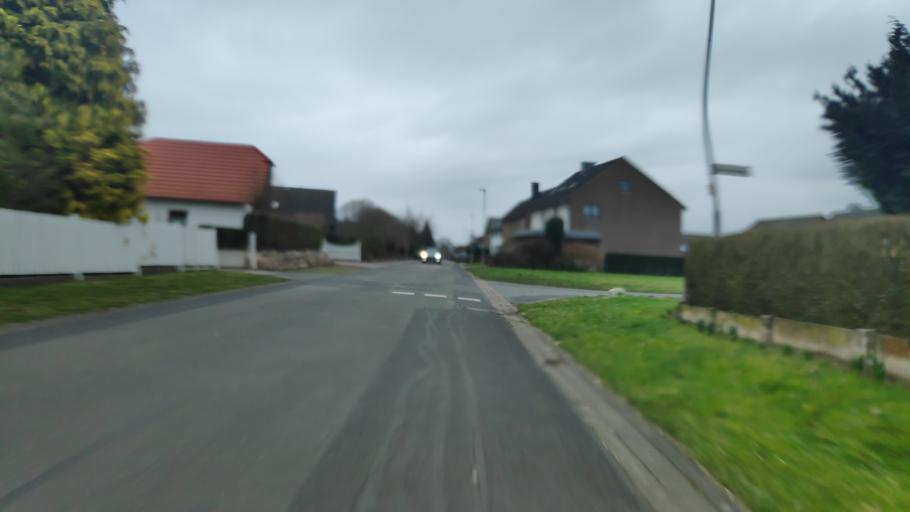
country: DE
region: North Rhine-Westphalia
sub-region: Regierungsbezirk Detmold
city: Minden
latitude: 52.3069
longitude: 8.8377
